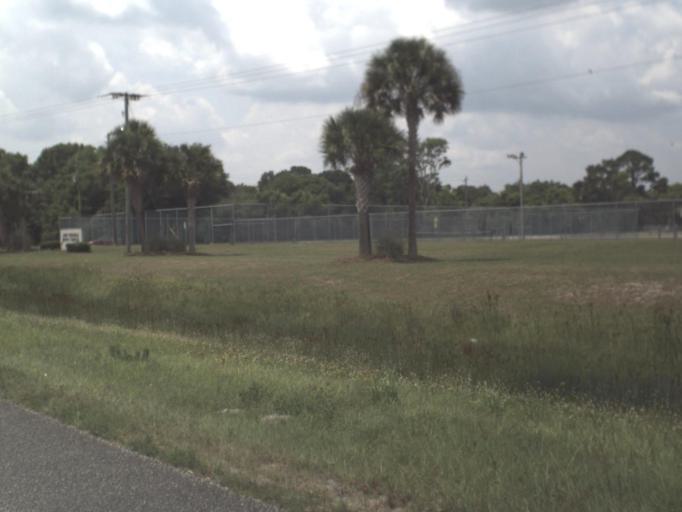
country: US
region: Florida
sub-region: Putnam County
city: Palatka
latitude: 29.6661
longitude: -81.6564
